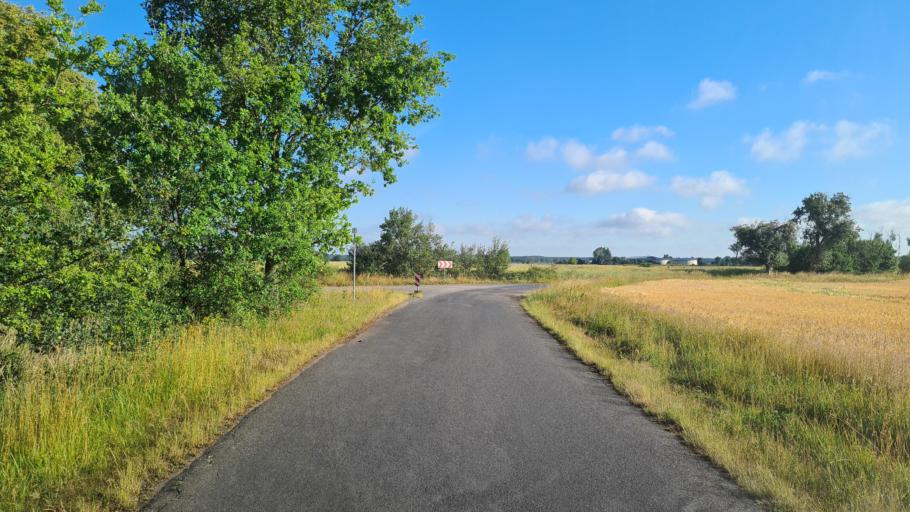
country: DE
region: Saxony
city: Beilrode
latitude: 51.6290
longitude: 13.1155
